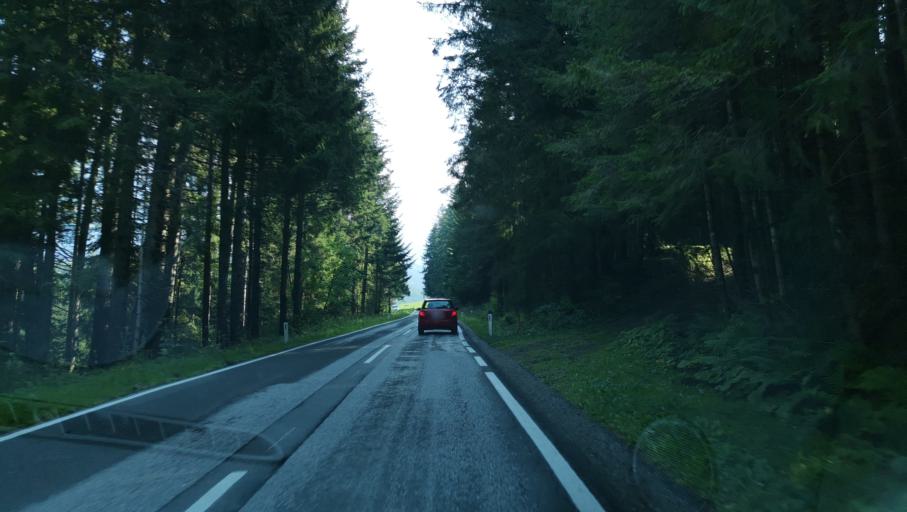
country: AT
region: Styria
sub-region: Politischer Bezirk Liezen
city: Trieben
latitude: 47.5254
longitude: 14.4603
